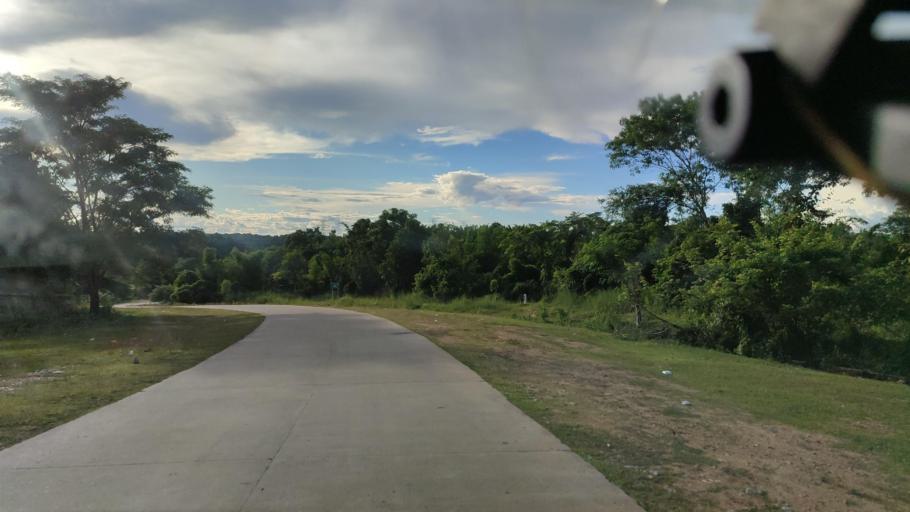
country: MM
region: Mandalay
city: Nay Pyi Taw
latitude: 19.9283
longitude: 95.9831
